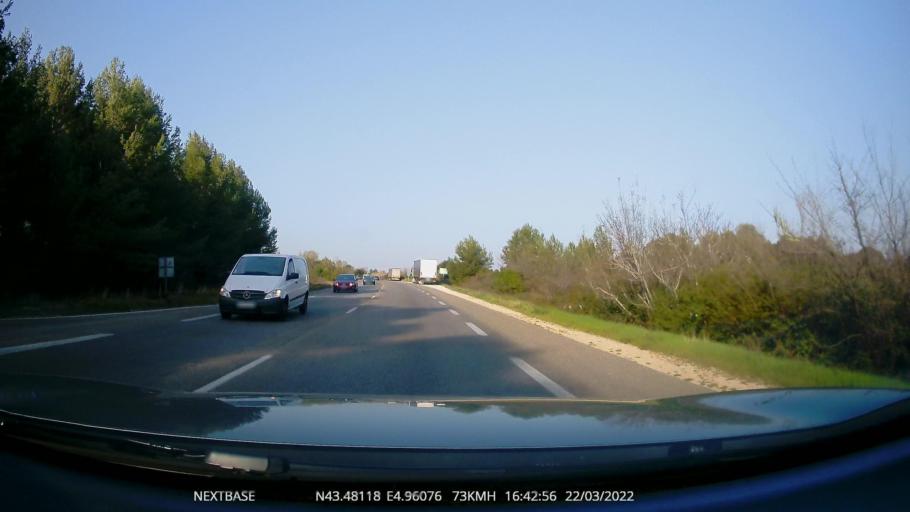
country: FR
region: Provence-Alpes-Cote d'Azur
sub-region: Departement des Bouches-du-Rhone
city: Istres
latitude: 43.4813
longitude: 4.9609
